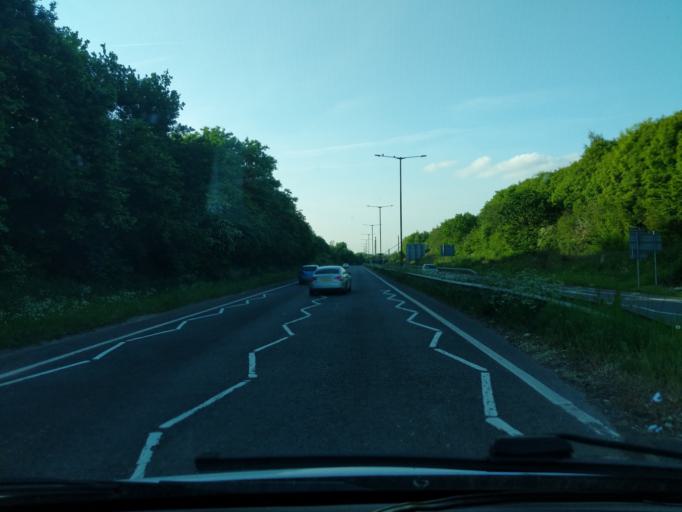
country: GB
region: England
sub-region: St. Helens
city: St Helens
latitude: 53.4290
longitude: -2.7401
